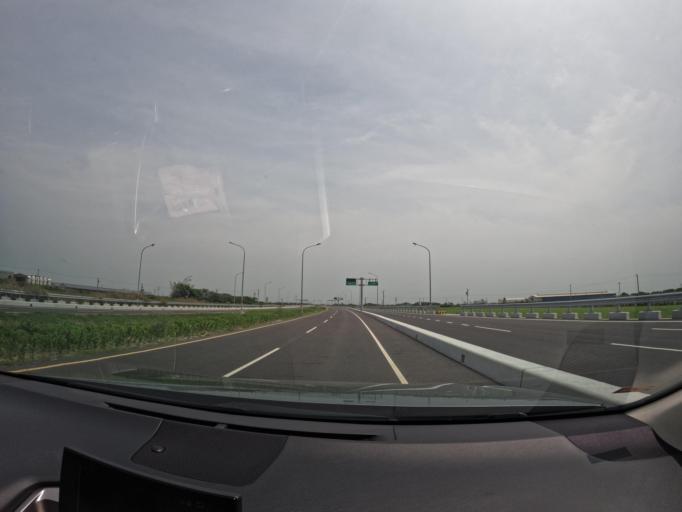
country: TW
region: Taiwan
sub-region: Changhua
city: Chang-hua
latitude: 23.9365
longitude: 120.3302
